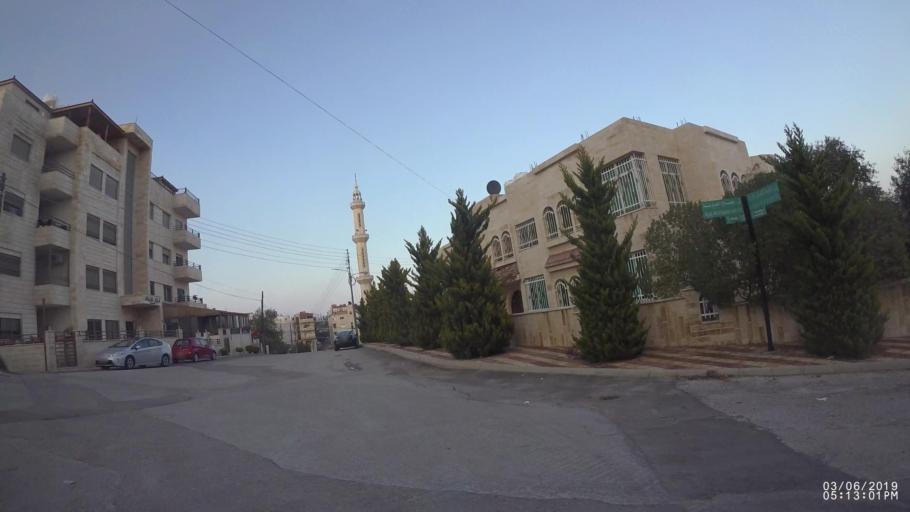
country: JO
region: Amman
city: Amman
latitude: 31.9923
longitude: 35.9520
